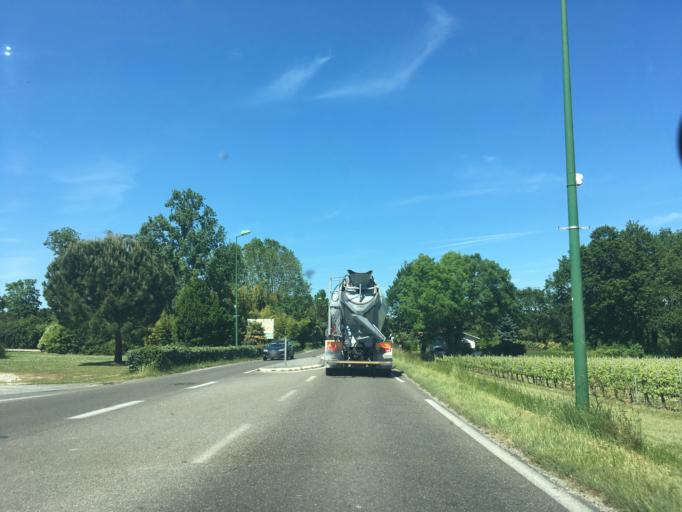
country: FR
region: Aquitaine
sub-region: Departement de la Gironde
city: Listrac-Medoc
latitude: 45.0700
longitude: -0.7939
